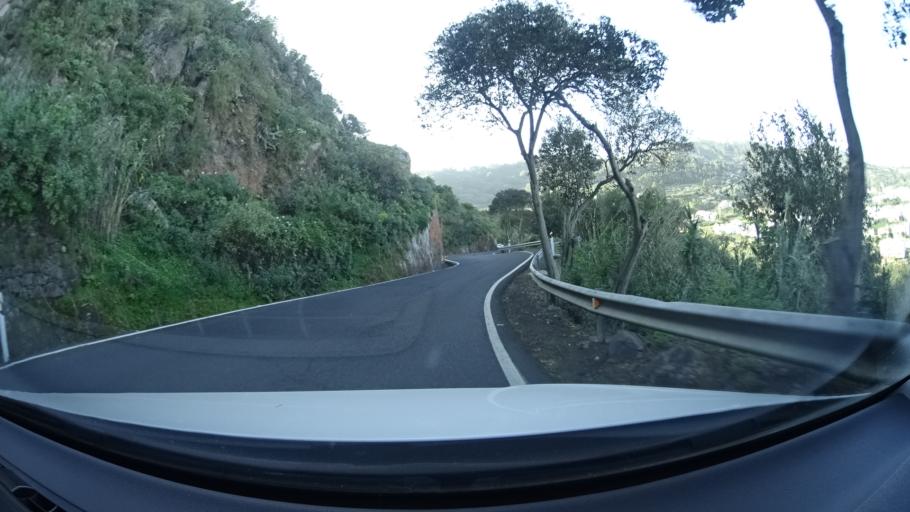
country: ES
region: Canary Islands
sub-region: Provincia de Las Palmas
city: Teror
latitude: 28.0547
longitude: -15.5543
